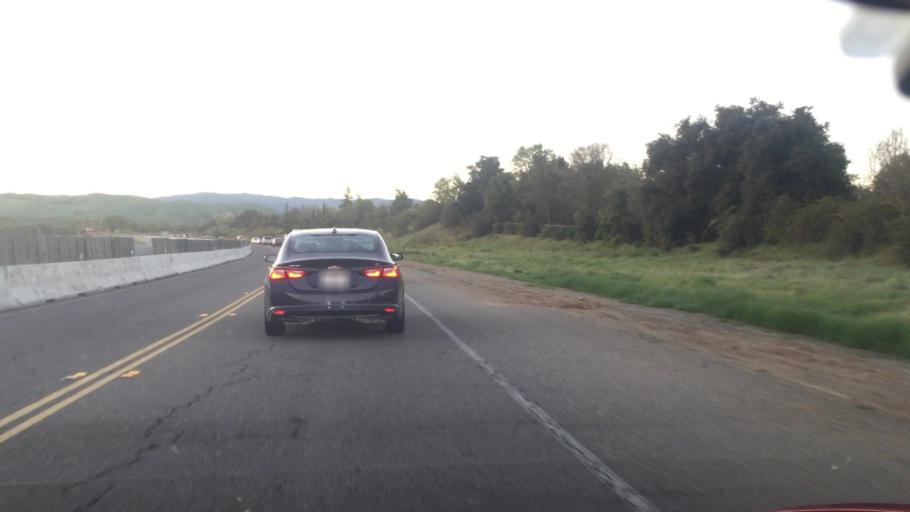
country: US
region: California
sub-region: Alameda County
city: Livermore
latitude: 37.6477
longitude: -121.8044
